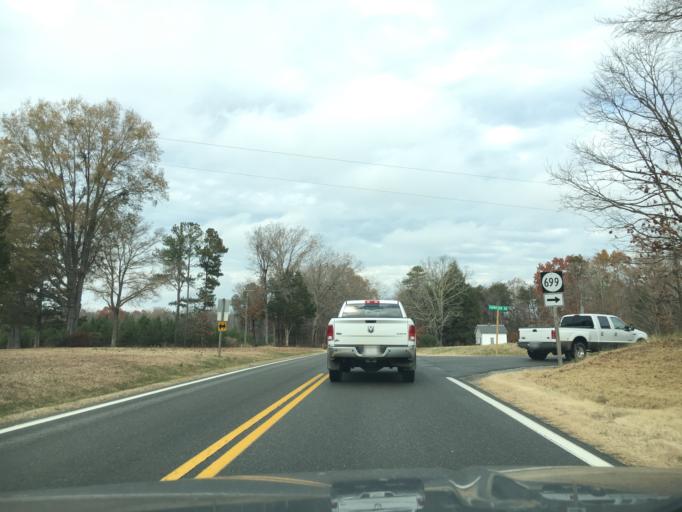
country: US
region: Virginia
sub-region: Prince Edward County
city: Farmville
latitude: 37.3863
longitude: -78.3721
